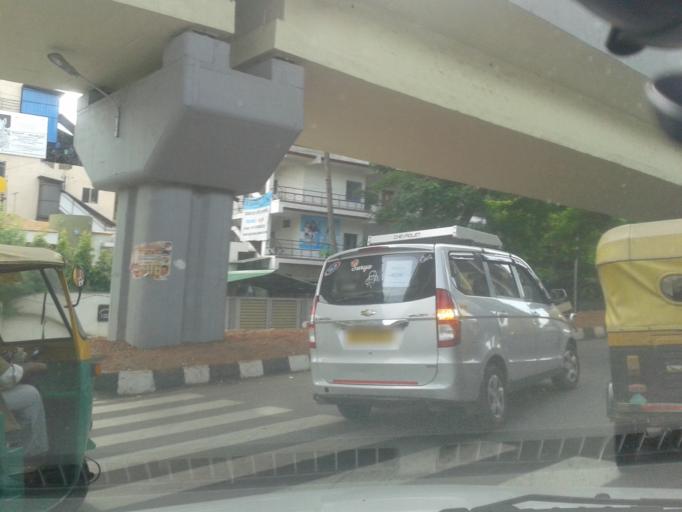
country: IN
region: Karnataka
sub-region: Bangalore Urban
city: Bangalore
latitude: 13.0040
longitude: 77.5491
